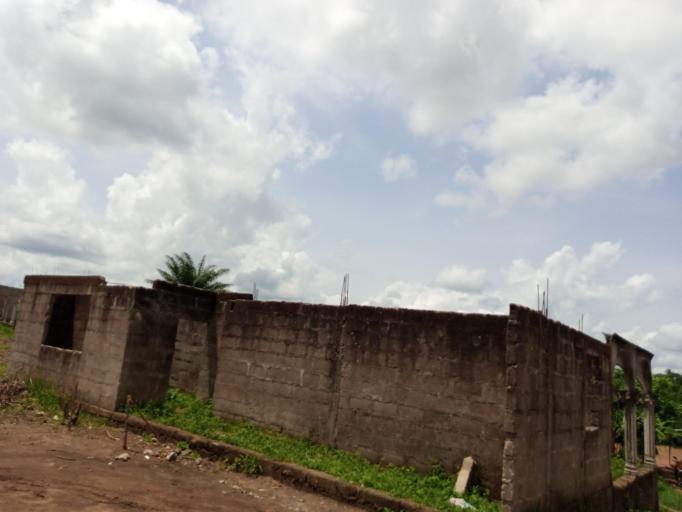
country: SL
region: Southern Province
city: Bo
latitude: 7.9397
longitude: -11.7208
